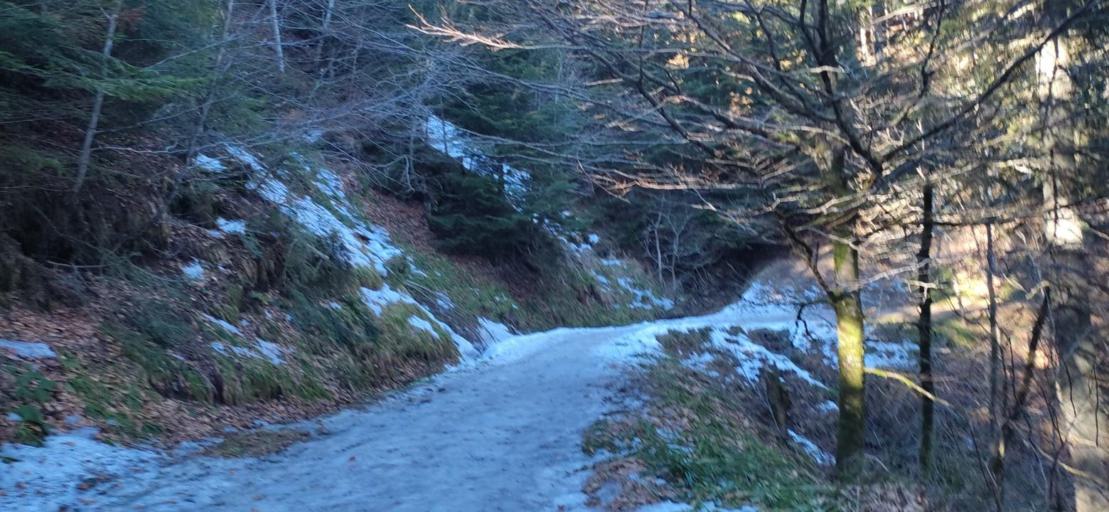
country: FR
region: Auvergne
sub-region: Departement du Puy-de-Dome
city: Mont-Dore
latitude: 45.5641
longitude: 2.8070
